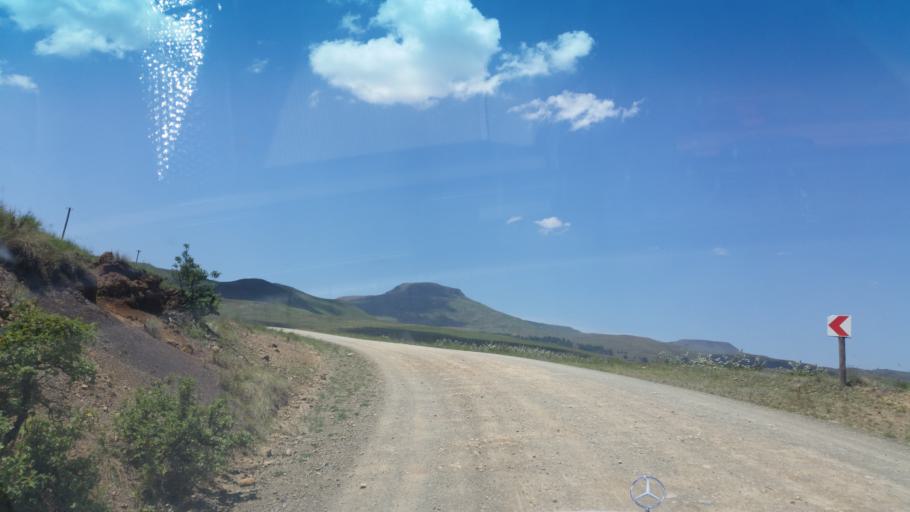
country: ZA
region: KwaZulu-Natal
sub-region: uMgungundlovu District Municipality
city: Impendle
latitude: -29.4558
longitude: 29.7452
